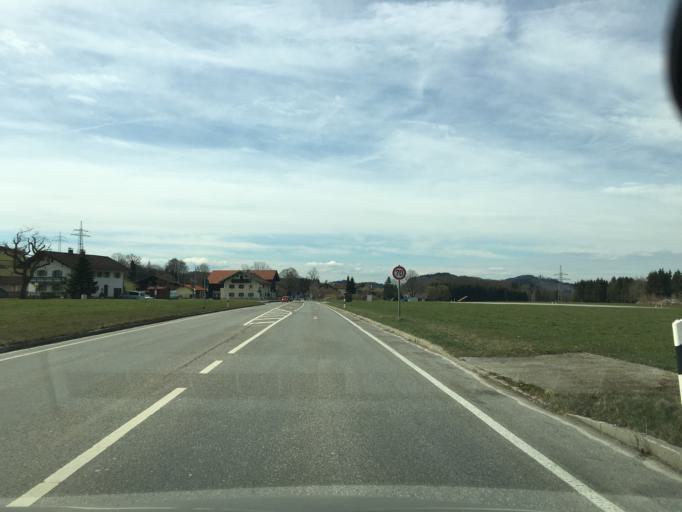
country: DE
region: Bavaria
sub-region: Upper Bavaria
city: Siegsdorf
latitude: 47.8193
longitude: 12.6686
